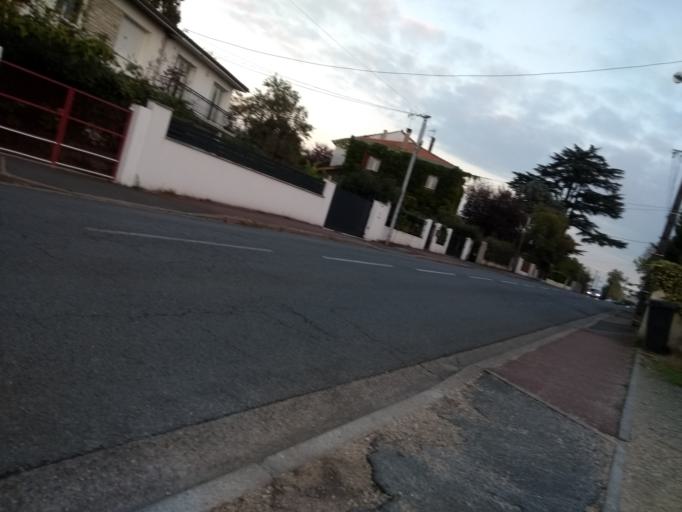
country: FR
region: Aquitaine
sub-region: Departement de la Gironde
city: Talence
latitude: 44.8060
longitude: -0.5849
